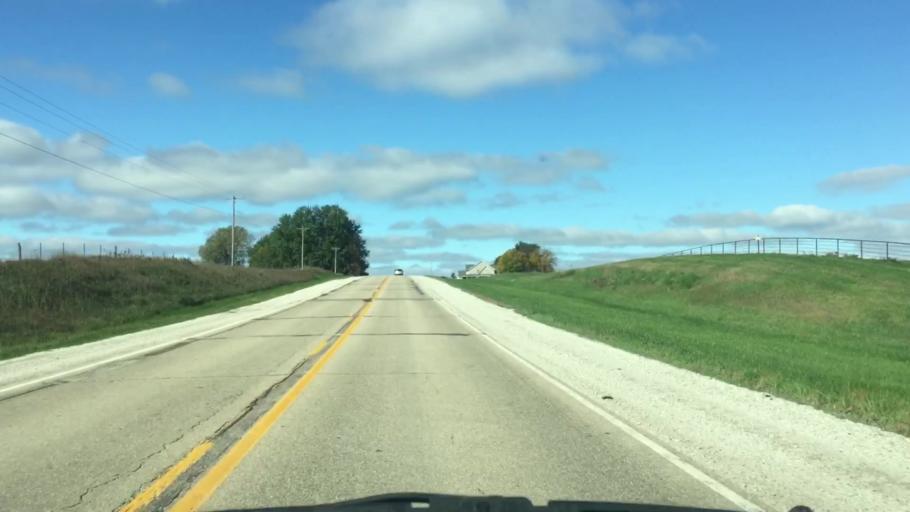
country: US
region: Iowa
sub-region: Decatur County
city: Leon
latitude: 40.7419
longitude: -93.8118
